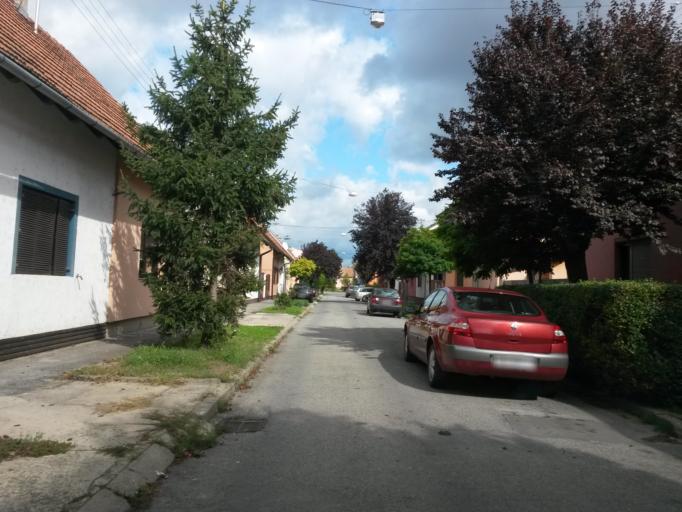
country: HR
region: Osjecko-Baranjska
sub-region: Grad Osijek
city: Osijek
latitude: 45.5492
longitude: 18.6851
